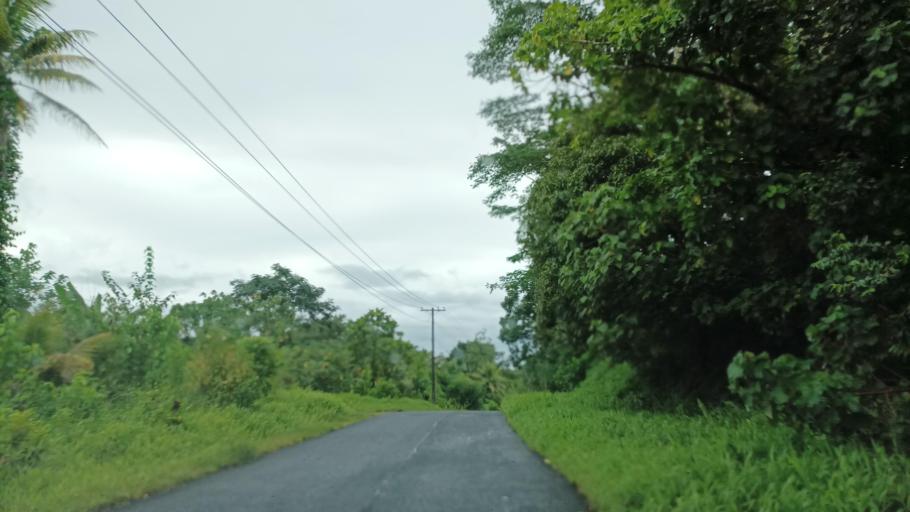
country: FM
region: Pohnpei
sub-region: Sokehs Municipality
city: Palikir - National Government Center
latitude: 6.8825
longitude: 158.1610
